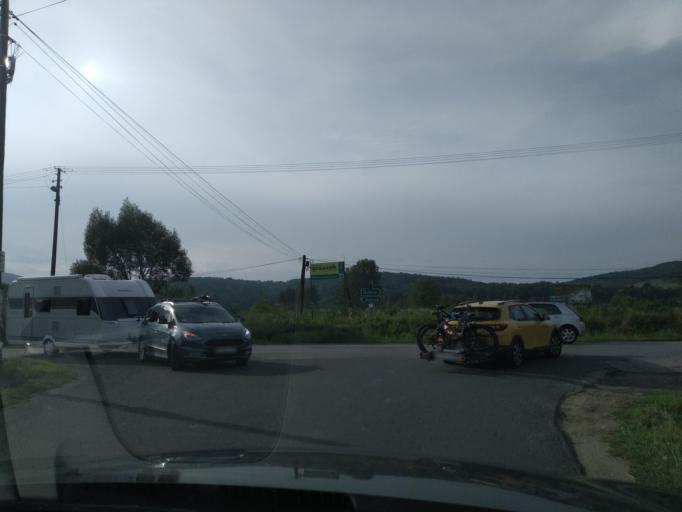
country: PL
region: Subcarpathian Voivodeship
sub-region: Powiat sanocki
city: Sanok
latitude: 49.6170
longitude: 22.2695
